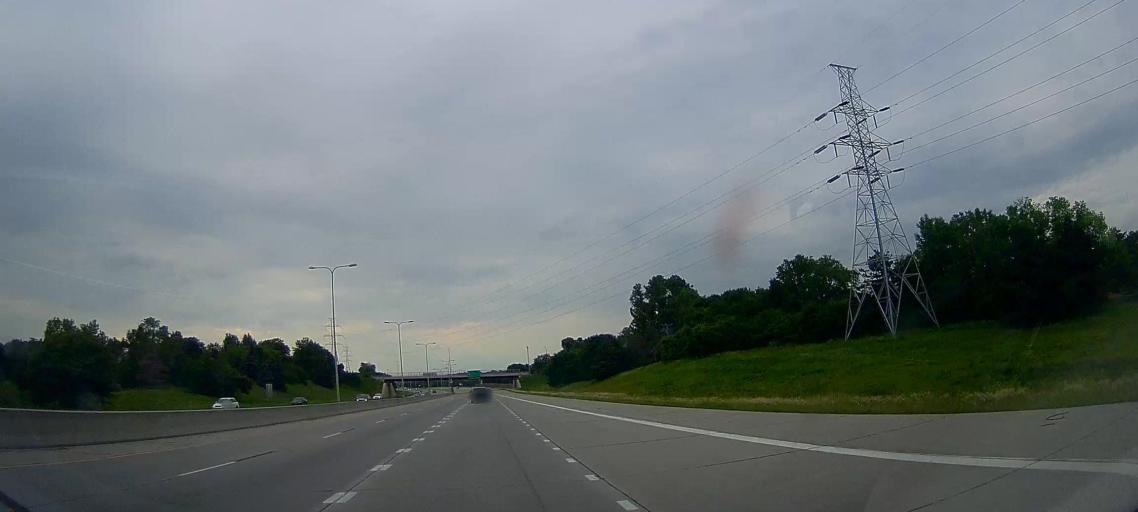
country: US
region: Nebraska
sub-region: Douglas County
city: Ralston
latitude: 41.2938
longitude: -96.0726
